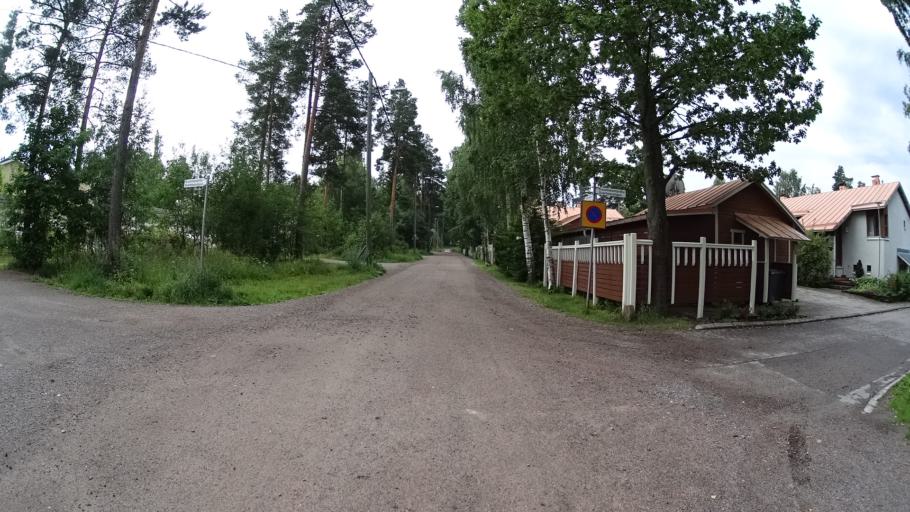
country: FI
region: Uusimaa
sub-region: Helsinki
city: Kilo
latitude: 60.2320
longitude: 24.8063
